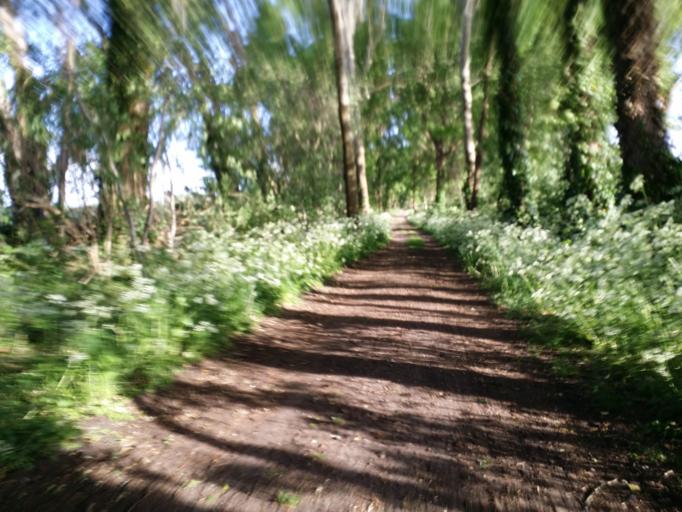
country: DE
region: Lower Saxony
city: Ganderkesee
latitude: 53.0164
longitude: 8.5506
